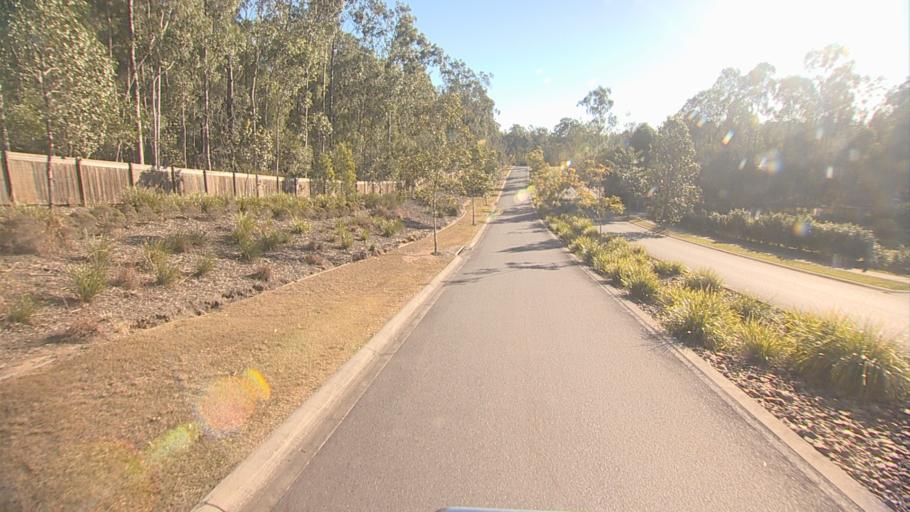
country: AU
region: Queensland
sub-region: Logan
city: North Maclean
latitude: -27.8230
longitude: 152.9802
